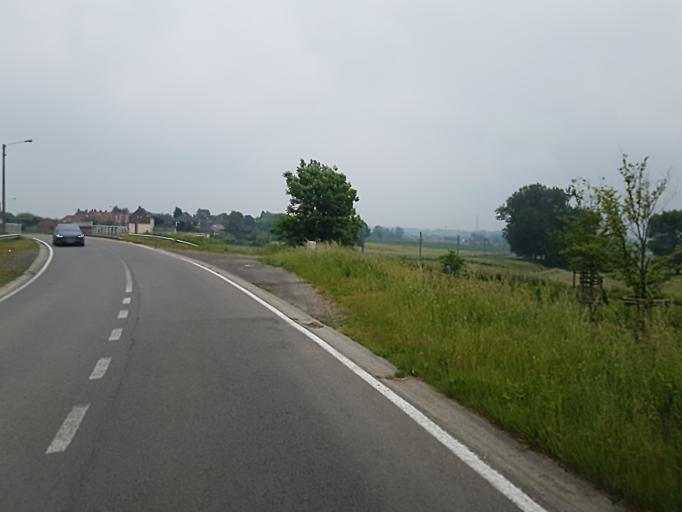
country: BE
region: Flanders
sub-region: Provincie West-Vlaanderen
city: Anzegem
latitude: 50.8282
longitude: 3.4697
